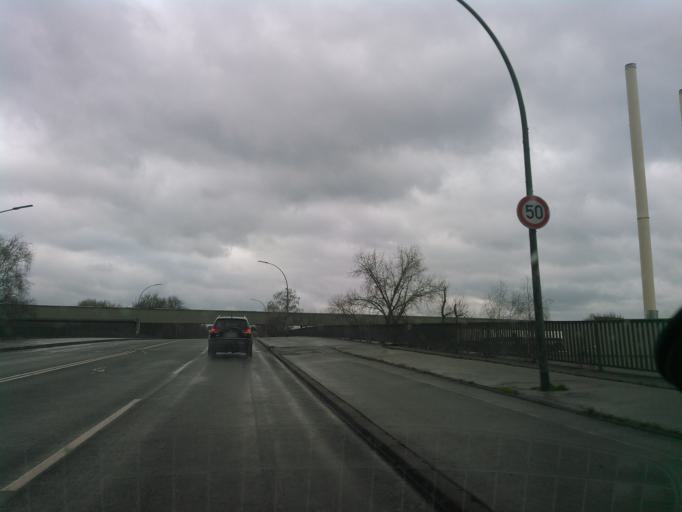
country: DE
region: North Rhine-Westphalia
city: Marl
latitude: 51.6000
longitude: 7.0688
